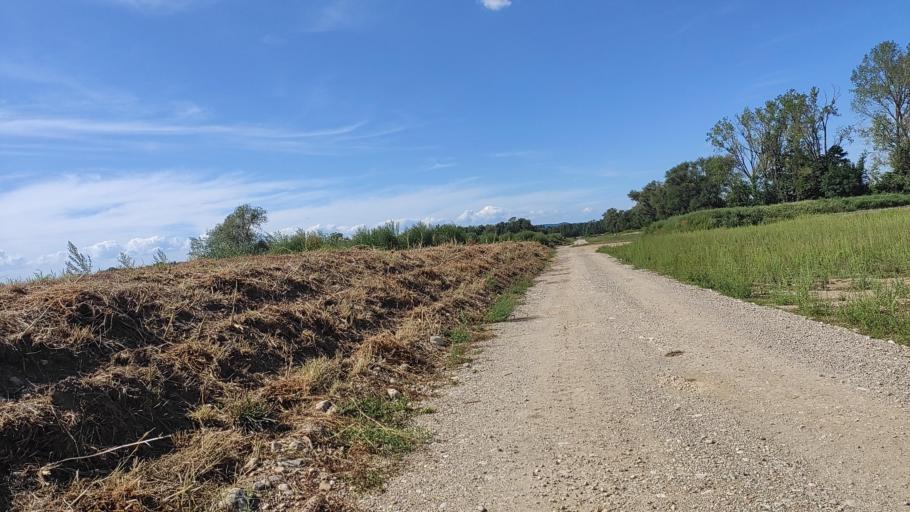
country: DE
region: Baden-Wuerttemberg
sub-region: Freiburg Region
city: Umkirch
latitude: 48.0074
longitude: 7.7960
